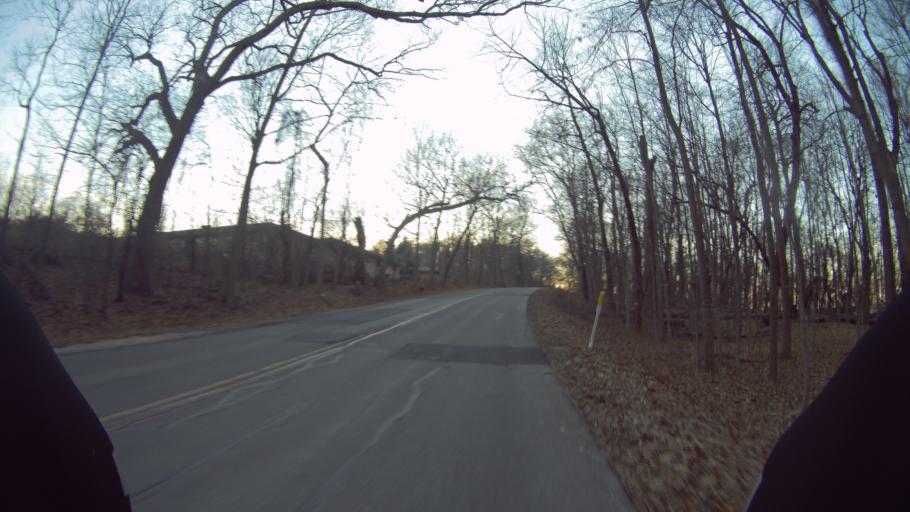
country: US
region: Wisconsin
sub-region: Dane County
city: Shorewood Hills
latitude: 43.0879
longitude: -89.4403
